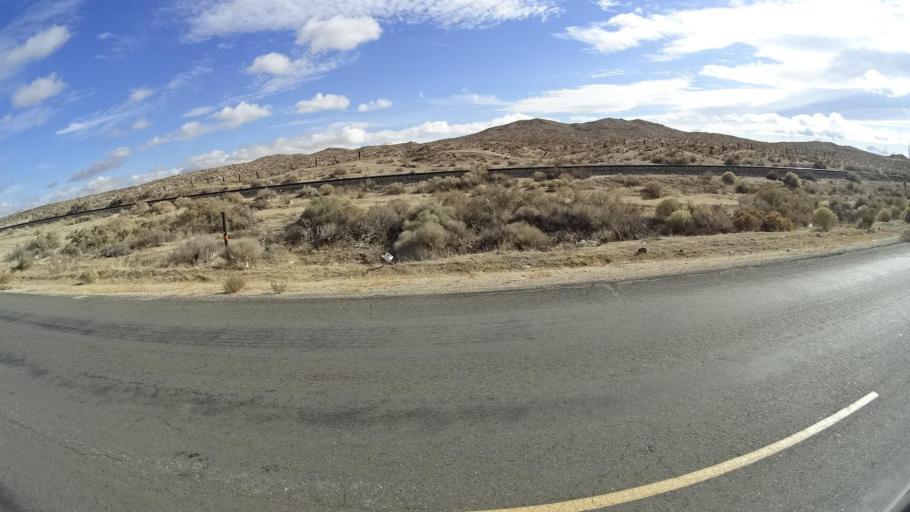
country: US
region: California
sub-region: Kern County
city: Rosamond
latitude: 34.8944
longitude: -118.1618
